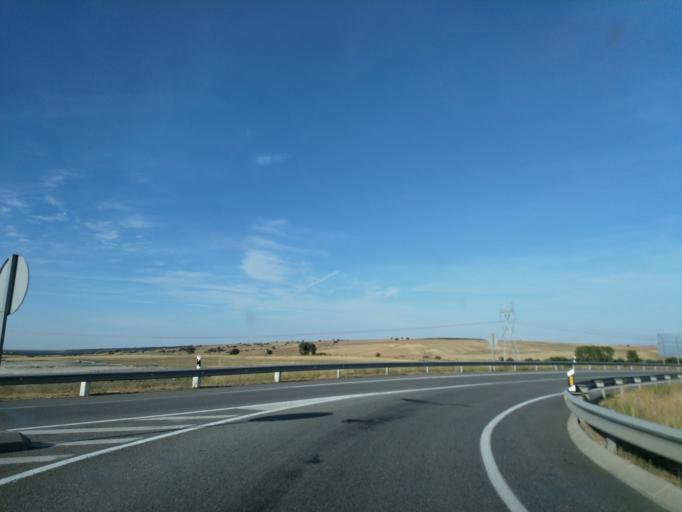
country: ES
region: Castille and Leon
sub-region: Provincia de Segovia
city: Villacastin
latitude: 40.7840
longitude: -4.4201
